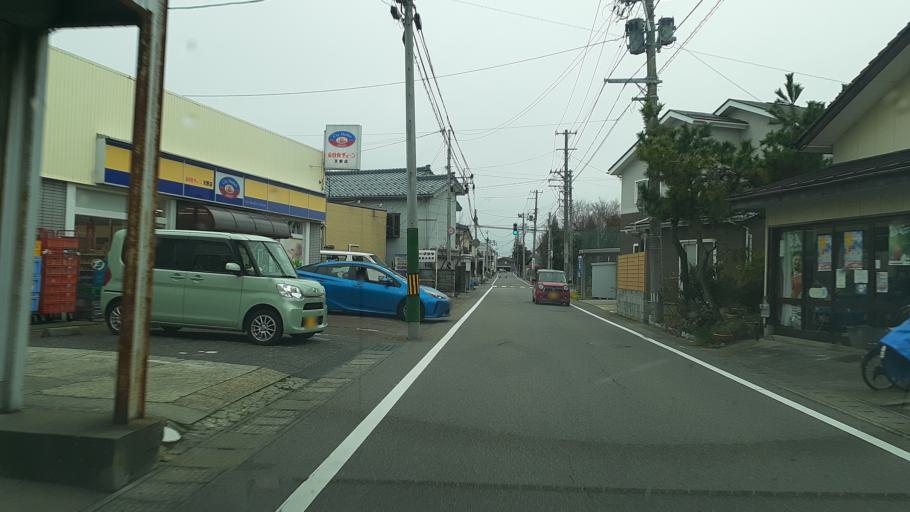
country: JP
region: Niigata
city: Niigata-shi
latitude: 37.8572
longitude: 139.0344
